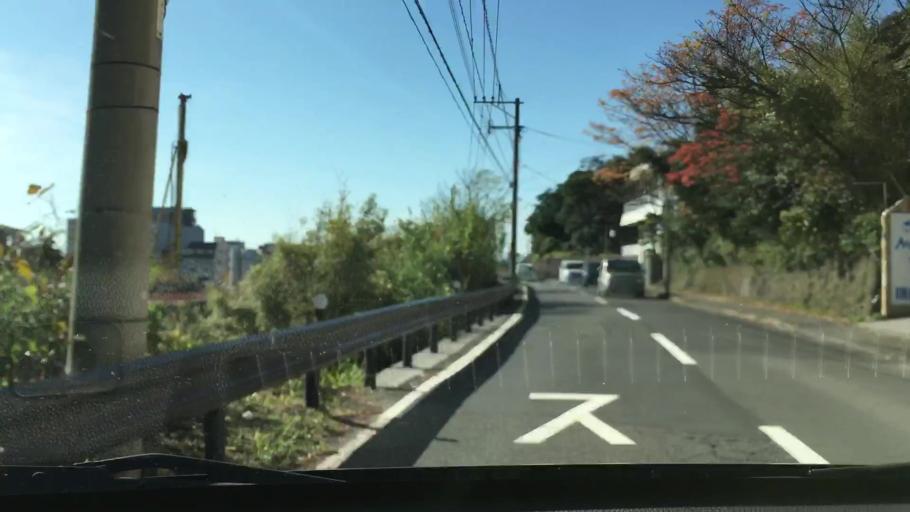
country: JP
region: Kagoshima
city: Kagoshima-shi
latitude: 31.6083
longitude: 130.5741
